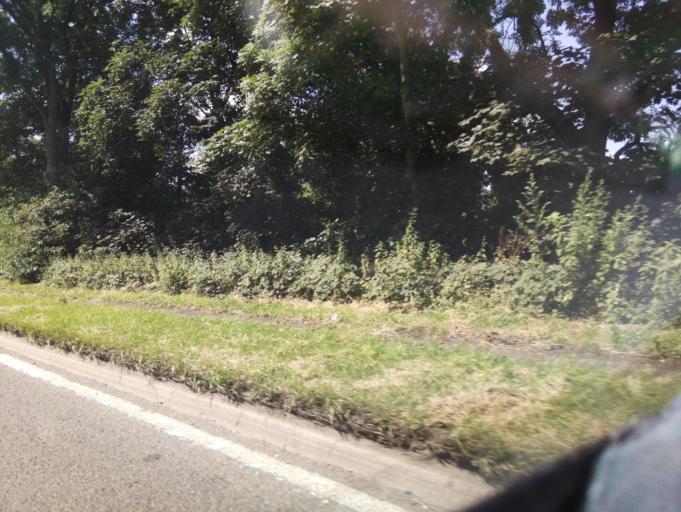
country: GB
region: England
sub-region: Warwickshire
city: Atherstone
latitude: 52.5807
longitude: -1.5575
